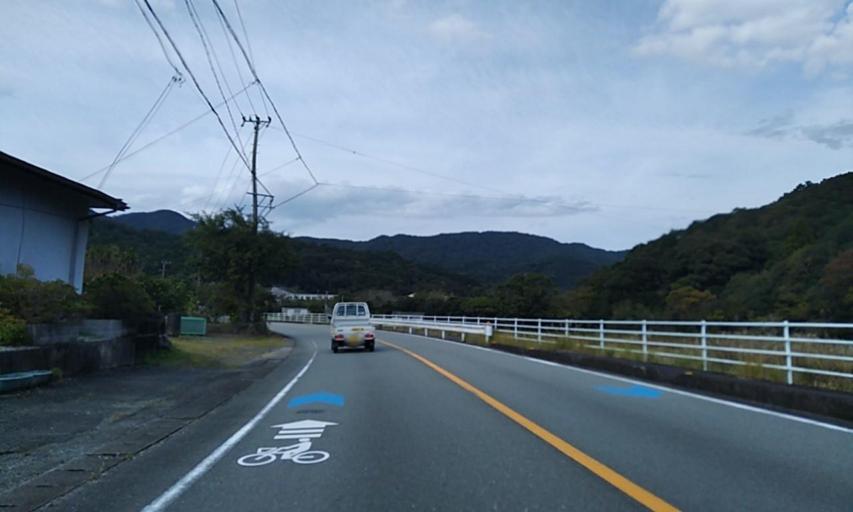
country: JP
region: Mie
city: Ise
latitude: 34.3043
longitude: 136.6368
